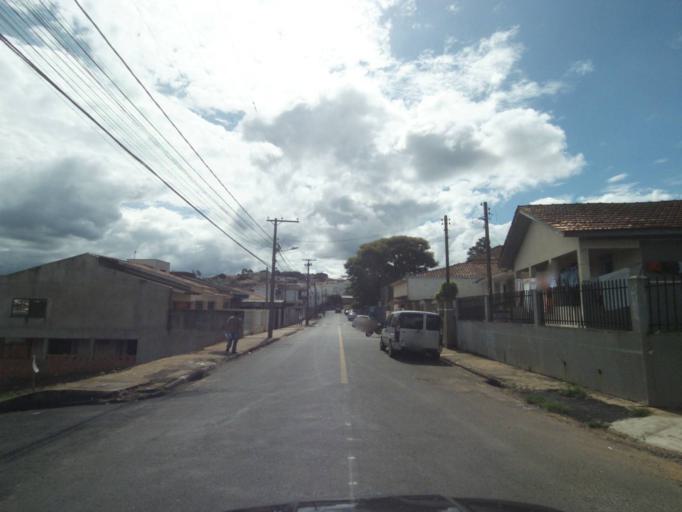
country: BR
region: Parana
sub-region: Telemaco Borba
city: Telemaco Borba
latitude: -24.3178
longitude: -50.6289
